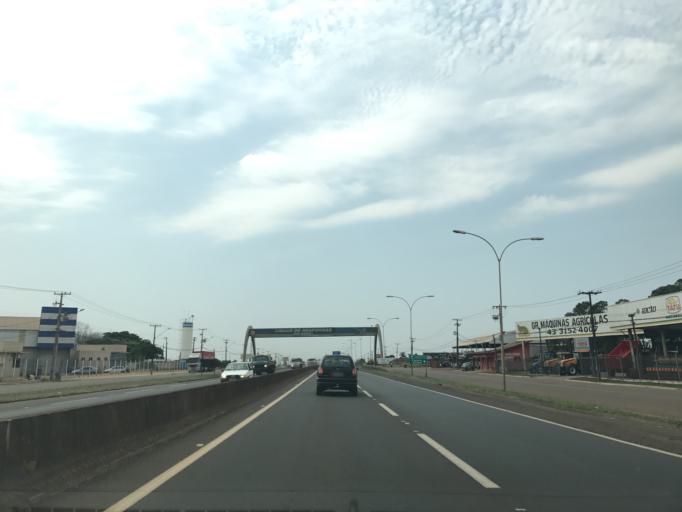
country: BR
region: Parana
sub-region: Arapongas
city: Arapongas
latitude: -23.3694
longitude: -51.4083
